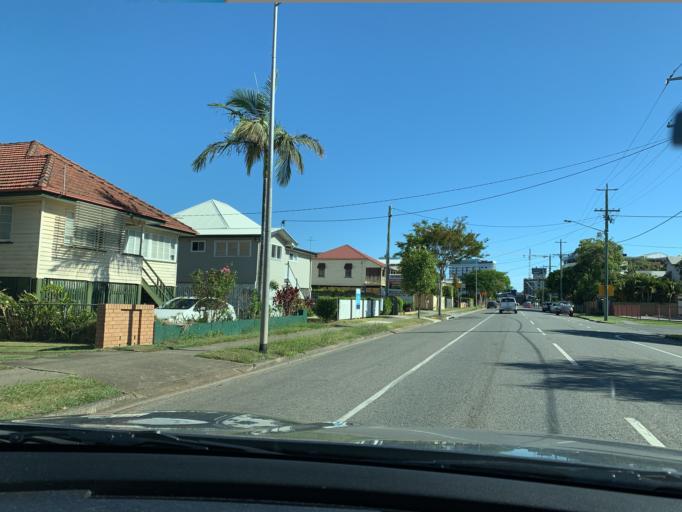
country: AU
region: Queensland
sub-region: Brisbane
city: Ascot
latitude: -27.4346
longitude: 153.0713
